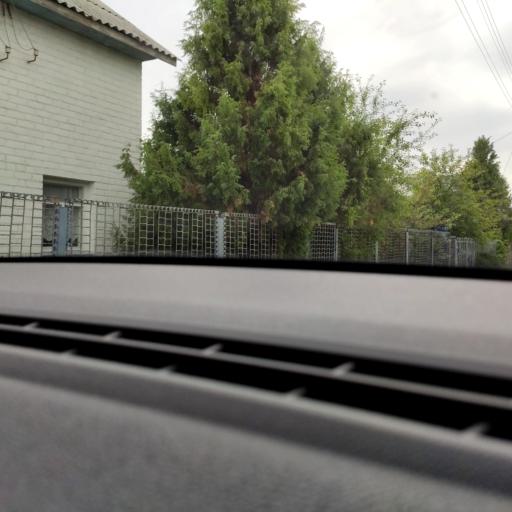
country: RU
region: Samara
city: Podstepki
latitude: 53.5054
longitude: 49.1609
